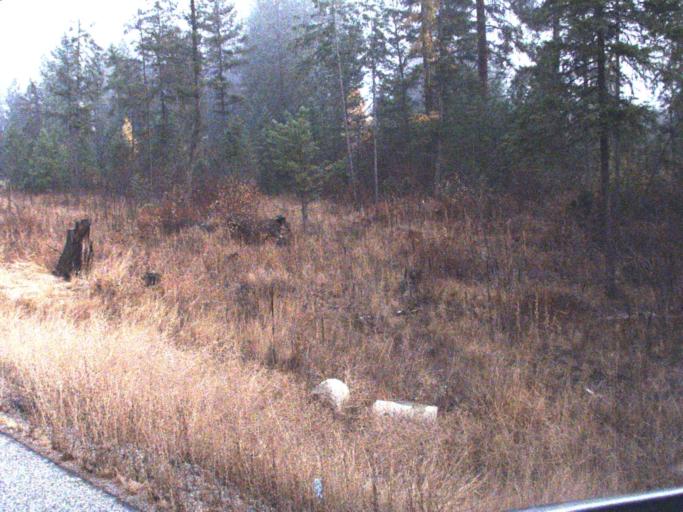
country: US
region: Washington
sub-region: Stevens County
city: Kettle Falls
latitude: 48.8411
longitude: -118.1993
